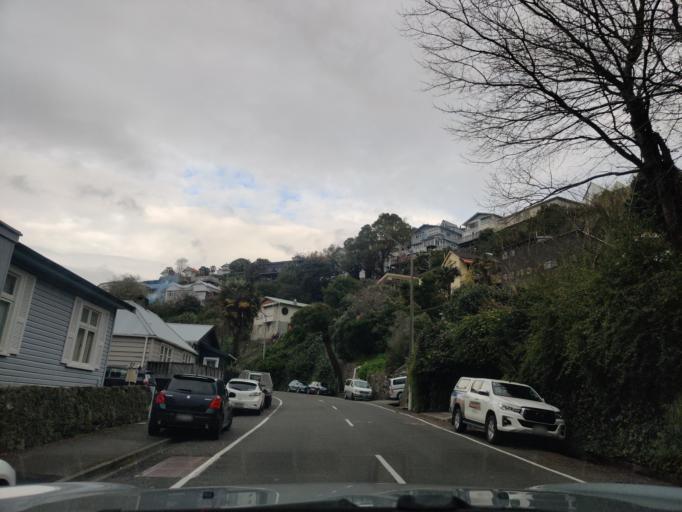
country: NZ
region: Hawke's Bay
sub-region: Napier City
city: Napier
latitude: -39.4837
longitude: 176.9101
